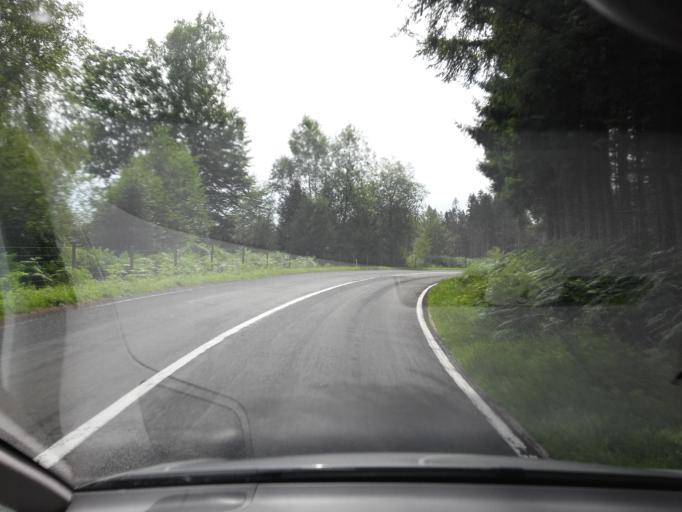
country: BE
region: Wallonia
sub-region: Province du Luxembourg
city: Chiny
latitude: 49.7814
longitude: 5.3489
